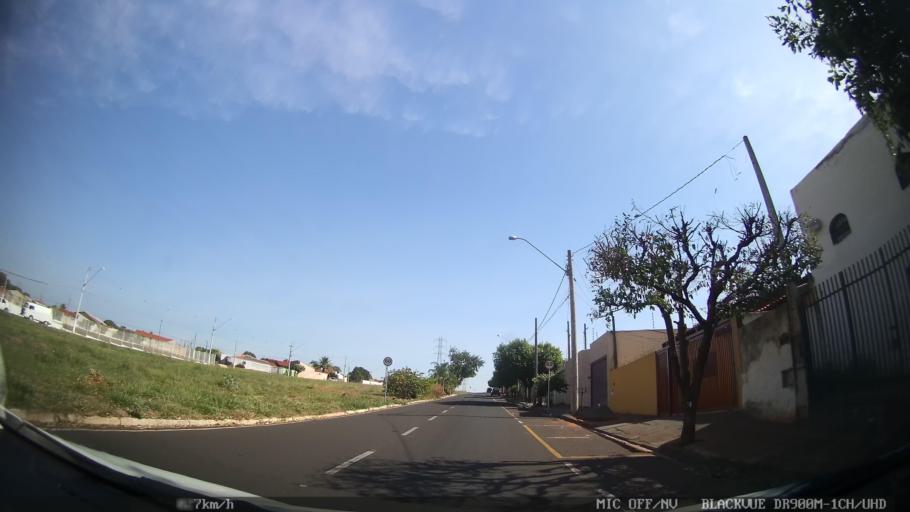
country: BR
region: Sao Paulo
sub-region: Sao Jose Do Rio Preto
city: Sao Jose do Rio Preto
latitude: -20.7889
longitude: -49.4148
